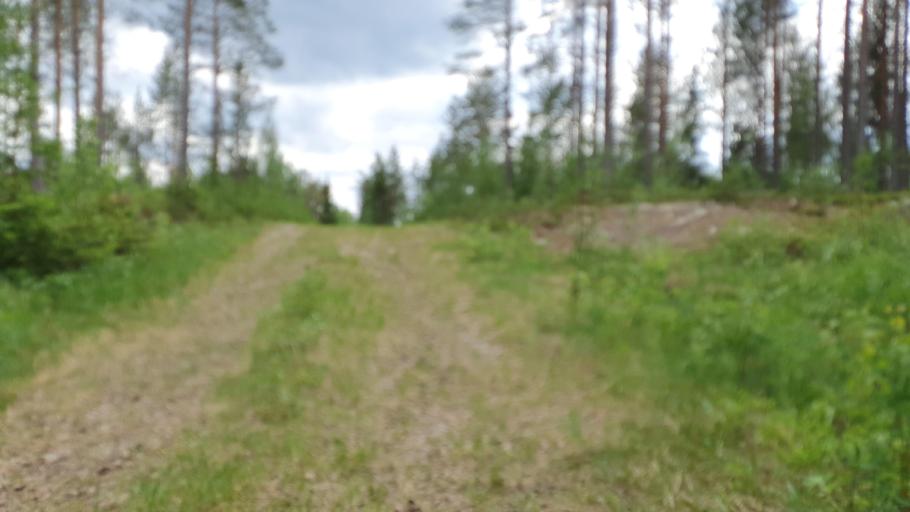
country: FI
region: Kainuu
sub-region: Kehys-Kainuu
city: Kuhmo
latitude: 64.4503
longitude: 29.6663
